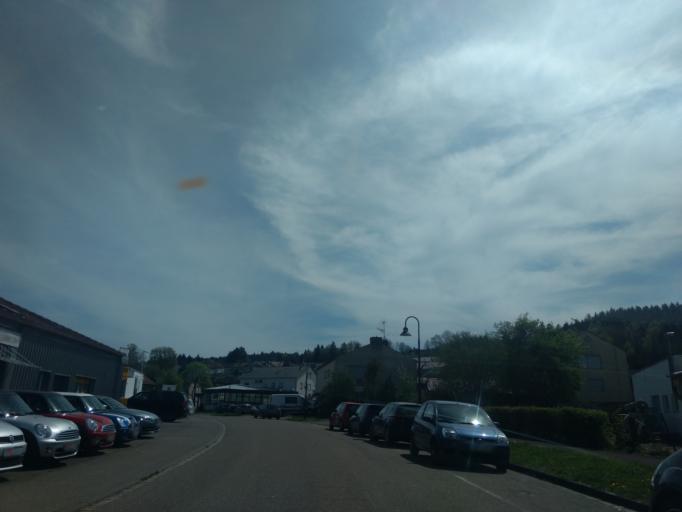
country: DE
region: Baden-Wuerttemberg
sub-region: Regierungsbezirk Stuttgart
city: Schwabisch Gmund
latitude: 48.7873
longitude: 9.7675
